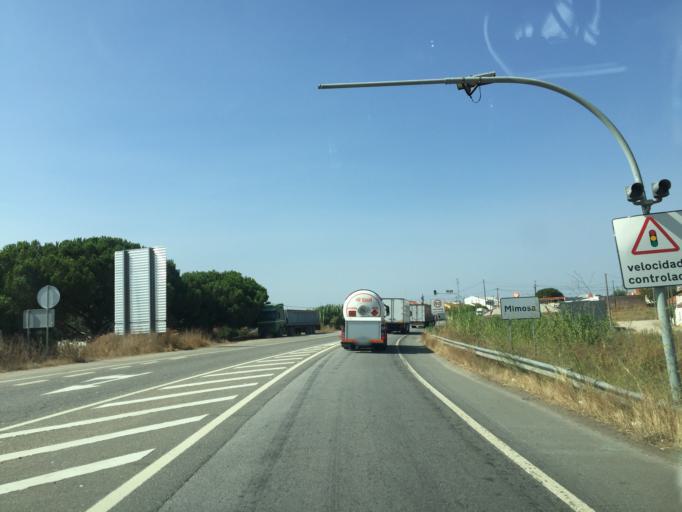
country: PT
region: Beja
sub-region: Aljustrel
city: Aljustrel
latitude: 37.9440
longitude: -8.3800
